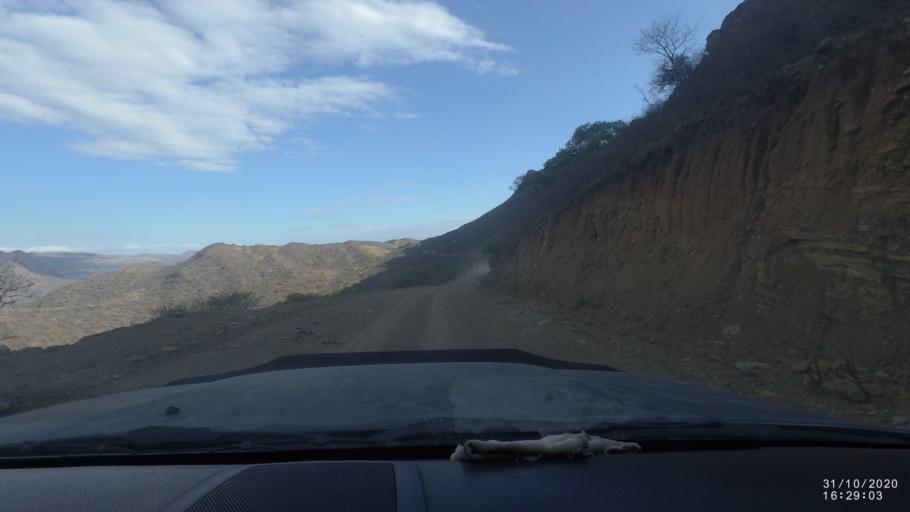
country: BO
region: Chuquisaca
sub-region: Provincia Zudanez
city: Mojocoya
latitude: -18.4169
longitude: -64.5862
